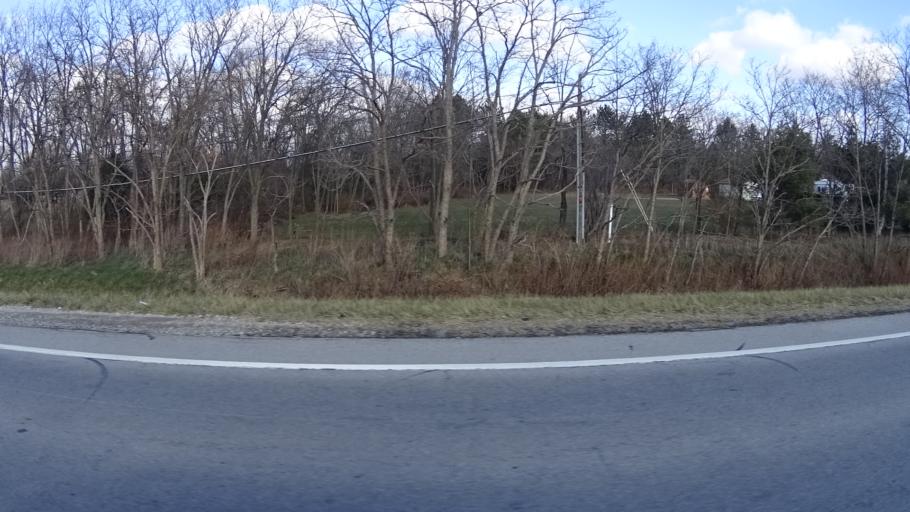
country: US
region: Ohio
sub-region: Lorain County
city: Camden
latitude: 41.2586
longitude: -82.3209
